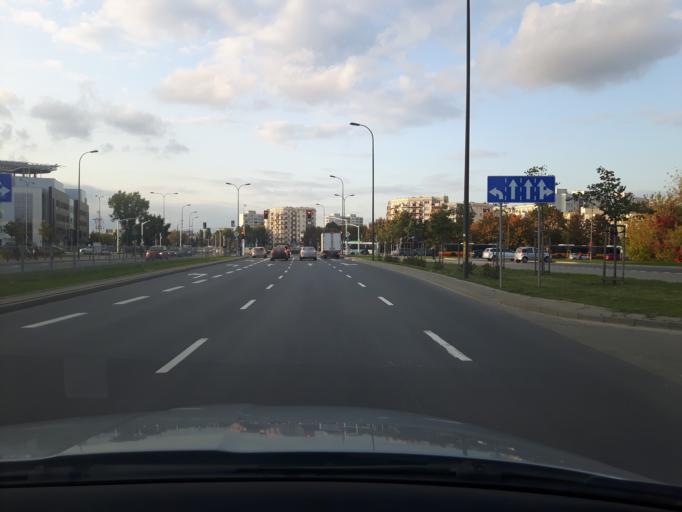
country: PL
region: Masovian Voivodeship
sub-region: Warszawa
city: Ursynow
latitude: 52.1451
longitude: 21.0379
